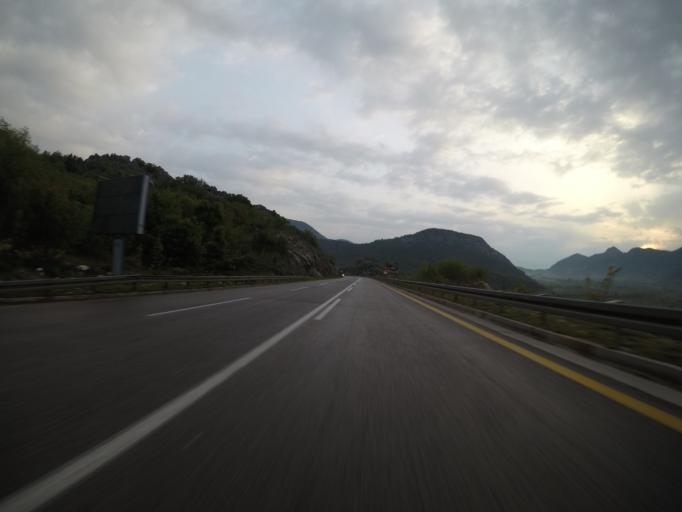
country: ME
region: Bar
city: Sutomore
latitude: 42.2173
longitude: 19.0506
